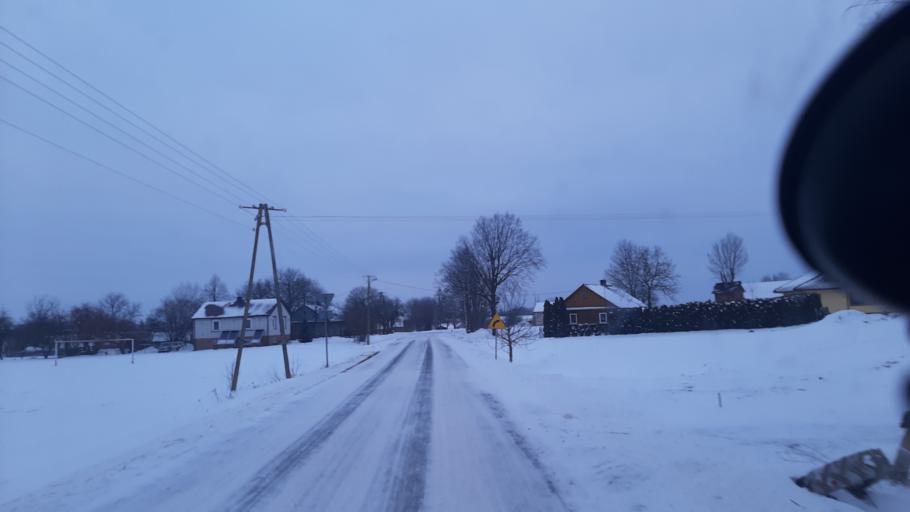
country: PL
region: Lublin Voivodeship
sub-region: Powiat lubelski
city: Jastkow
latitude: 51.3445
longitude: 22.4108
